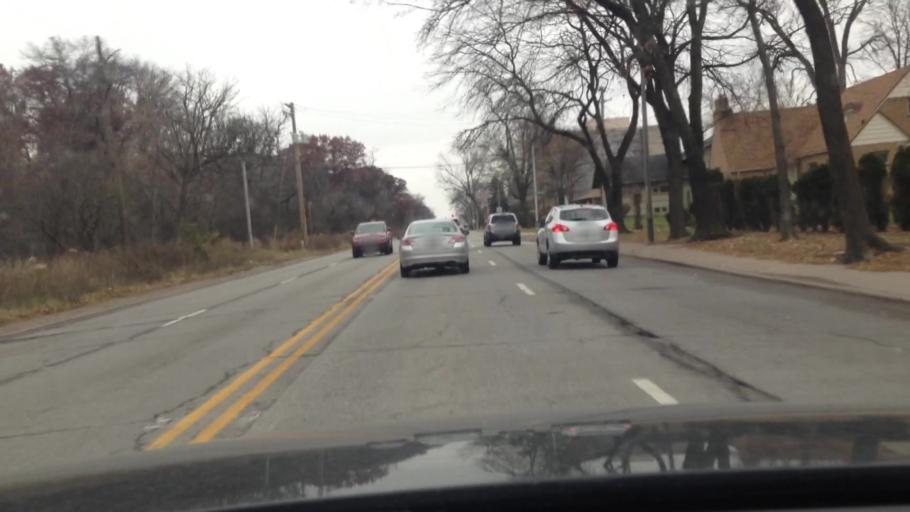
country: US
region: Illinois
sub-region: Cook County
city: Maywood
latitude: 41.8860
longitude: -87.8343
